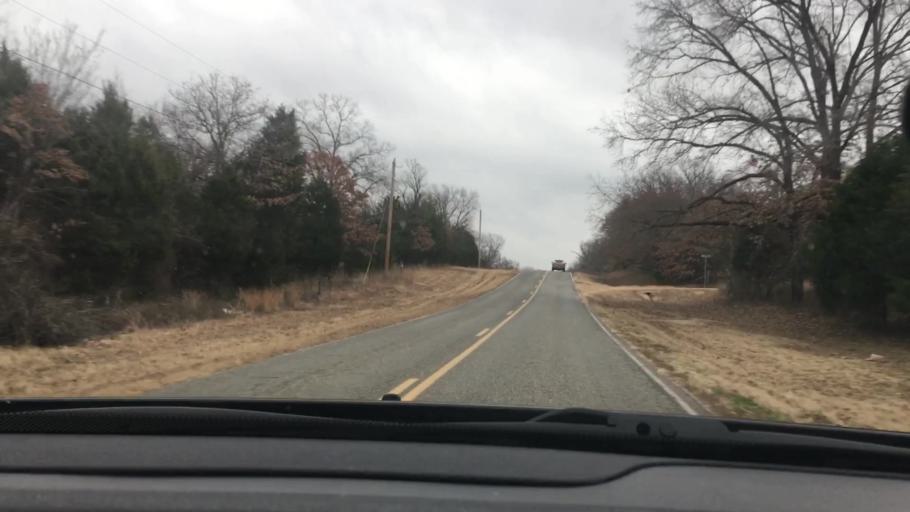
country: US
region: Oklahoma
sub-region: Johnston County
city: Tishomingo
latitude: 34.2087
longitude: -96.5934
